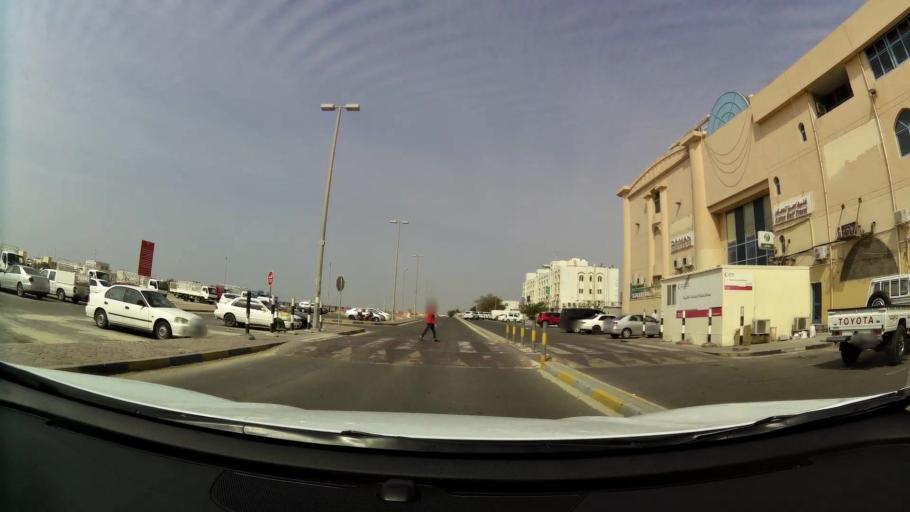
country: AE
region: Abu Dhabi
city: Abu Dhabi
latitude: 24.5552
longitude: 54.6939
